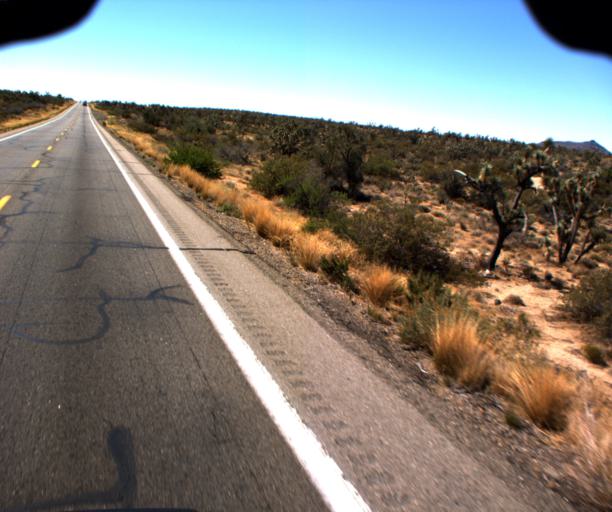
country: US
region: Arizona
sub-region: Yavapai County
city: Congress
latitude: 34.2532
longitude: -113.0837
